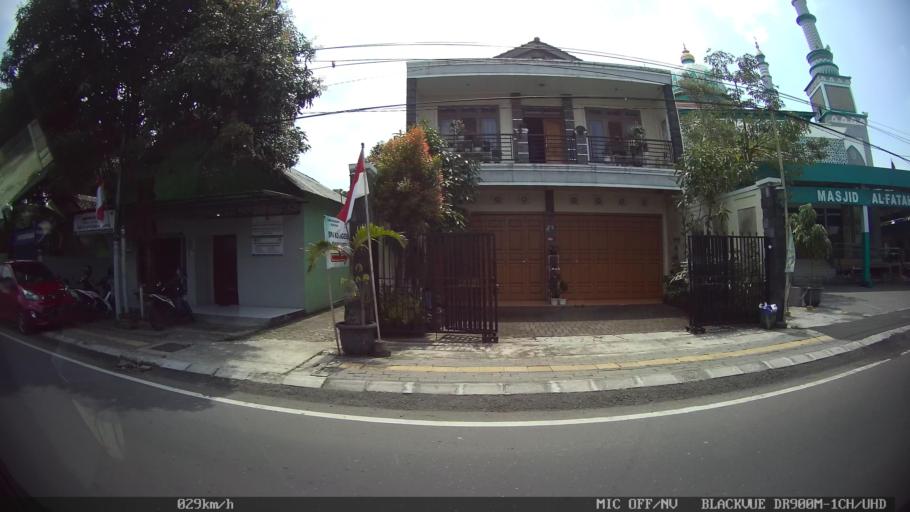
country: ID
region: Daerah Istimewa Yogyakarta
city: Yogyakarta
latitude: -7.8102
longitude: 110.3978
